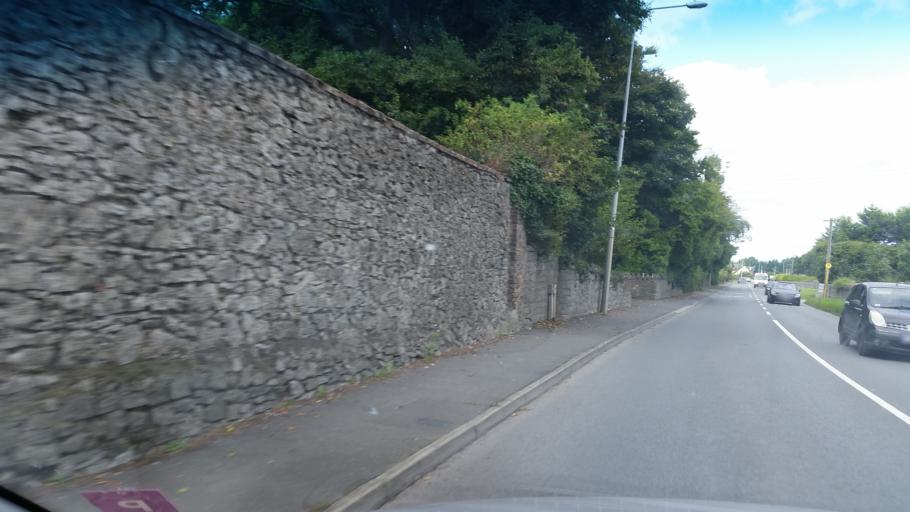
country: IE
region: Leinster
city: Kinsealy-Drinan
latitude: 53.4285
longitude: -6.1779
